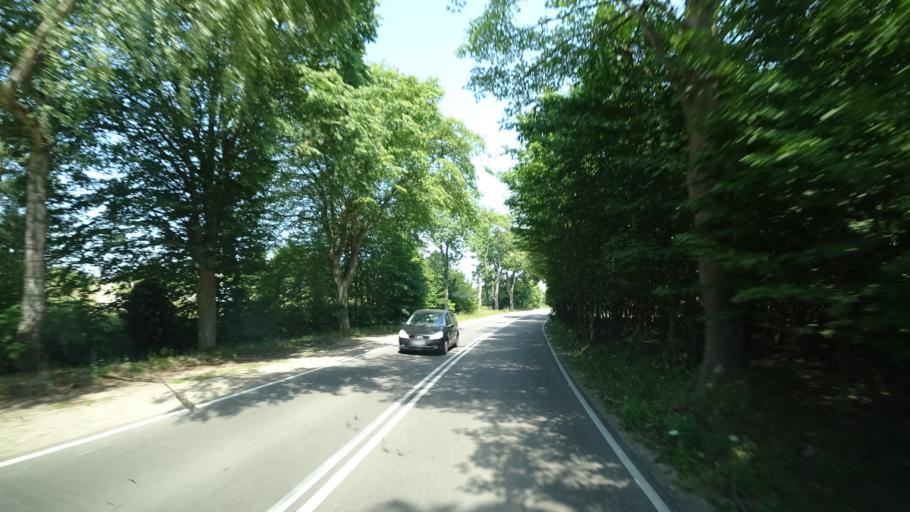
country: PL
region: Pomeranian Voivodeship
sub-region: Powiat koscierski
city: Dziemiany
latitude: 53.9979
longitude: 17.7674
